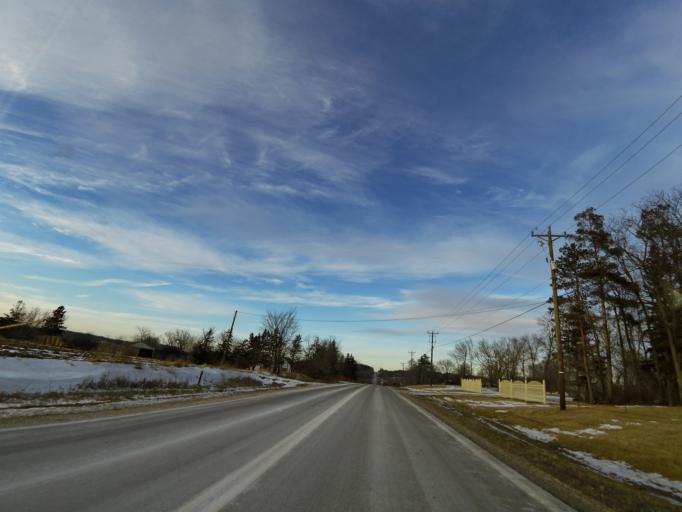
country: US
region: Minnesota
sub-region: Washington County
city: Afton
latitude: 44.9099
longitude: -92.8429
